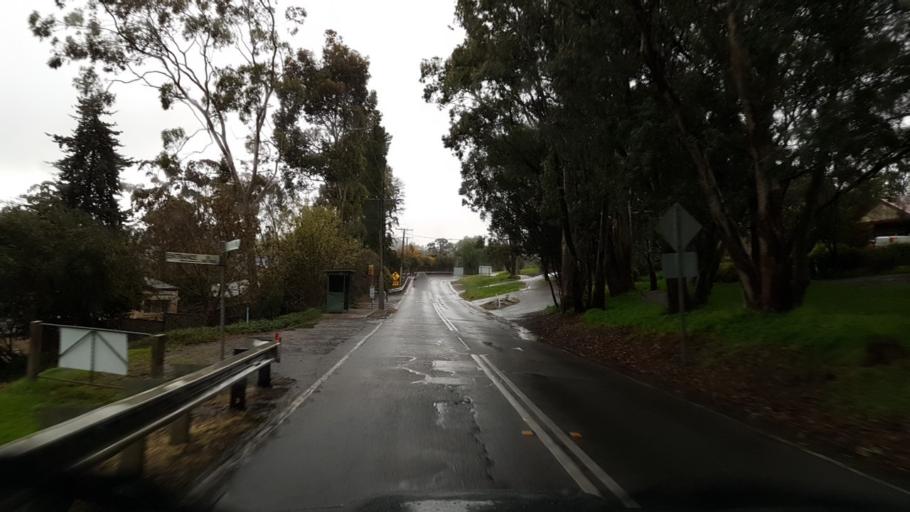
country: AU
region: South Australia
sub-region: Onkaparinga
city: Craigburn Farm
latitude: -35.0509
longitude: 138.6200
